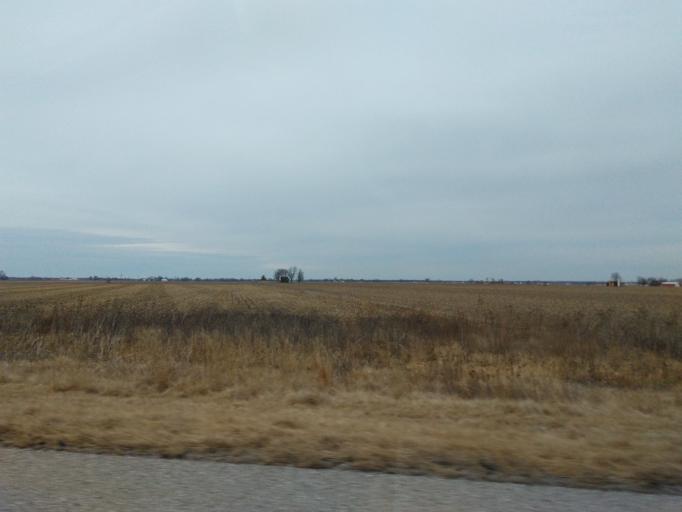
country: US
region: Illinois
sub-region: Clinton County
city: New Baden
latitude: 38.5136
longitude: -89.6563
